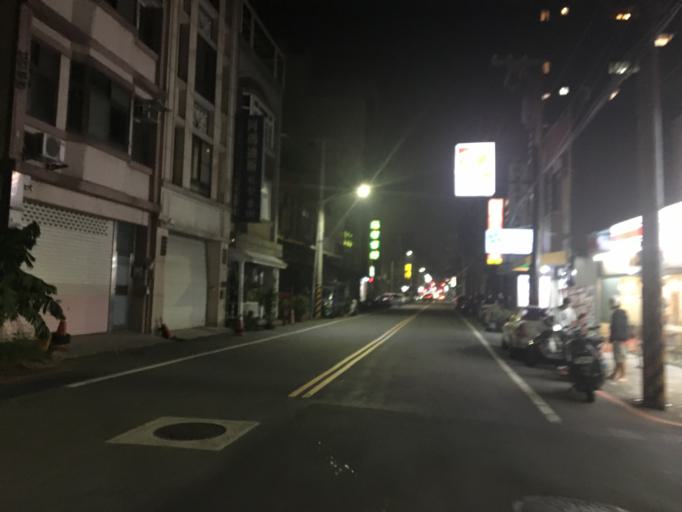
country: TW
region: Taiwan
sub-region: Hsinchu
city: Hsinchu
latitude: 24.8212
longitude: 120.9772
